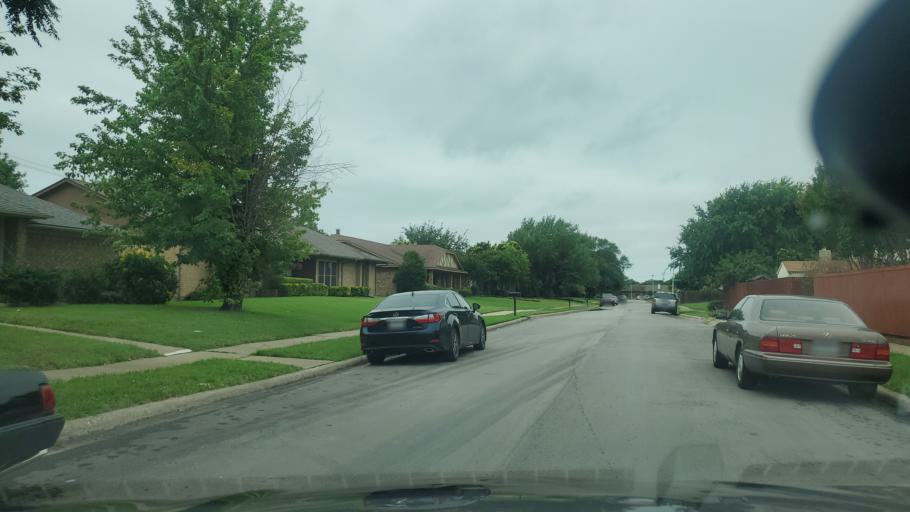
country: US
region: Texas
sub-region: Dallas County
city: Garland
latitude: 32.9367
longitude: -96.6276
